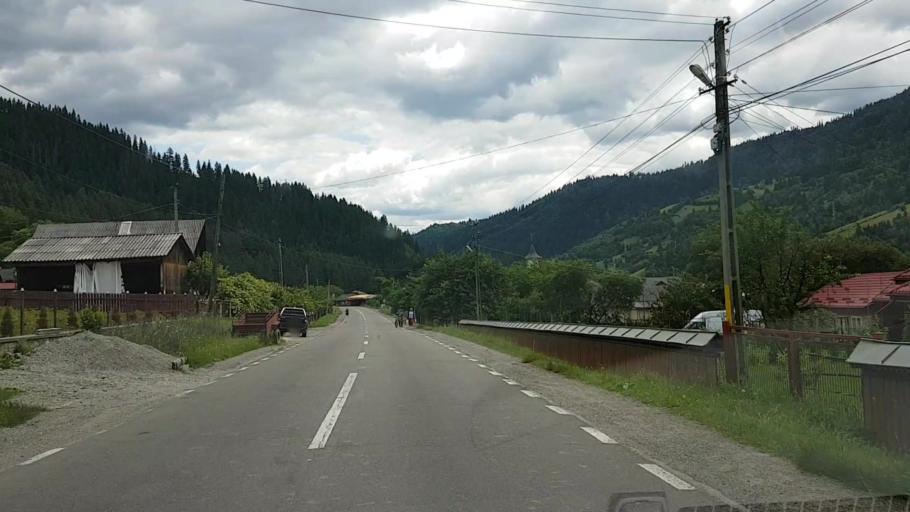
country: RO
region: Neamt
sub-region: Comuna Poiana Teiului
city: Poiana Teiului
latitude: 47.1298
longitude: 25.9013
